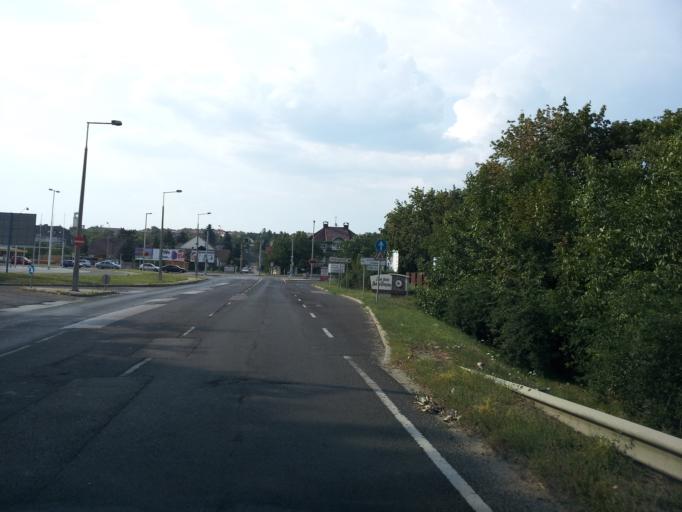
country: HU
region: Budapest
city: Budapest XXII. keruelet
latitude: 47.4099
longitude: 19.0233
